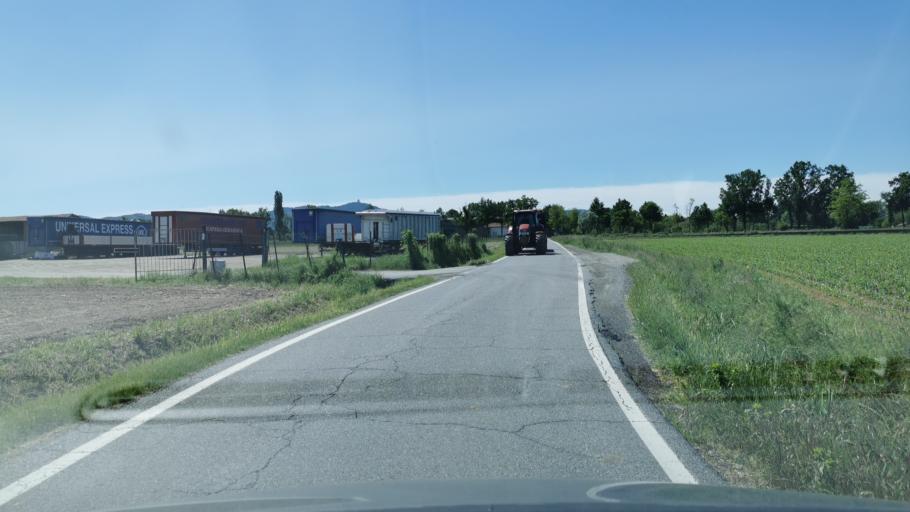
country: IT
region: Piedmont
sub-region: Provincia di Torino
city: Leini
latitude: 45.1673
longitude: 7.7429
